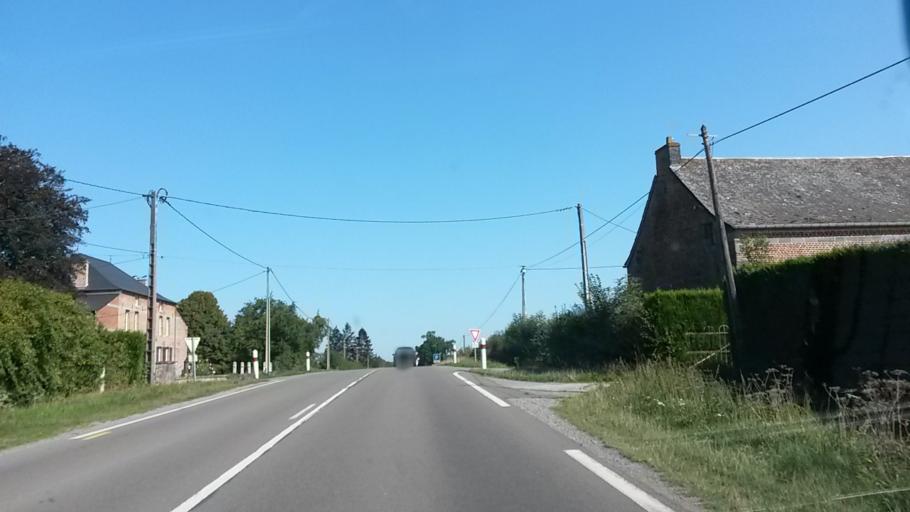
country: FR
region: Nord-Pas-de-Calais
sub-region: Departement du Nord
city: Avesnes-sur-Helpe
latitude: 50.0932
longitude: 3.9304
